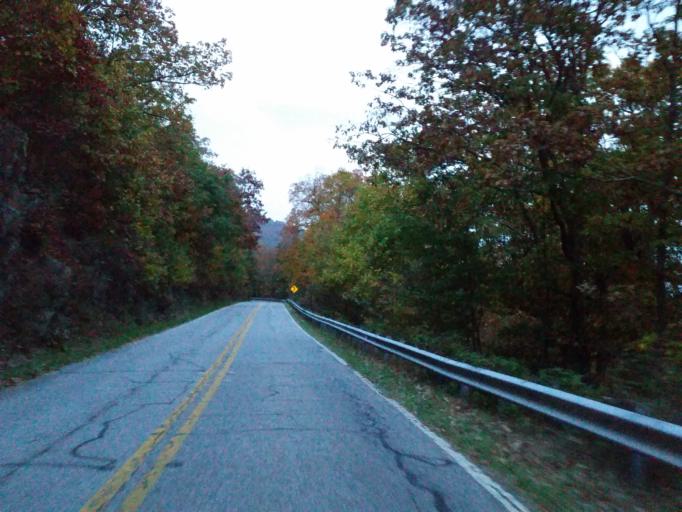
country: US
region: Georgia
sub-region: Lumpkin County
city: Dahlonega
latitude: 34.6616
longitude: -83.9784
